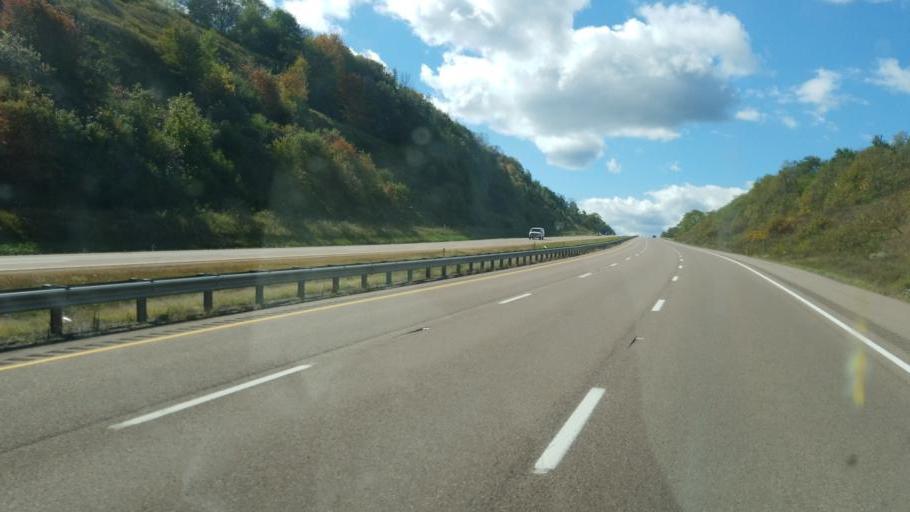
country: US
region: Pennsylvania
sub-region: Somerset County
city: Meyersdale
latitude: 39.7000
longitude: -79.2871
